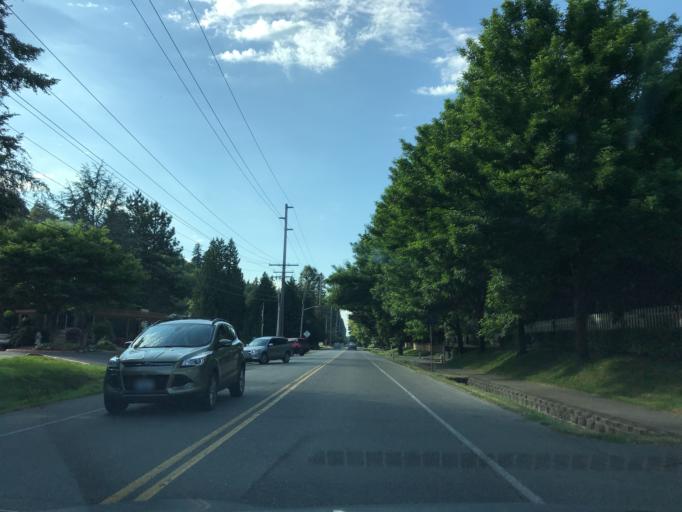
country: US
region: Washington
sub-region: King County
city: Issaquah
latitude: 47.5315
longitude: -122.0423
